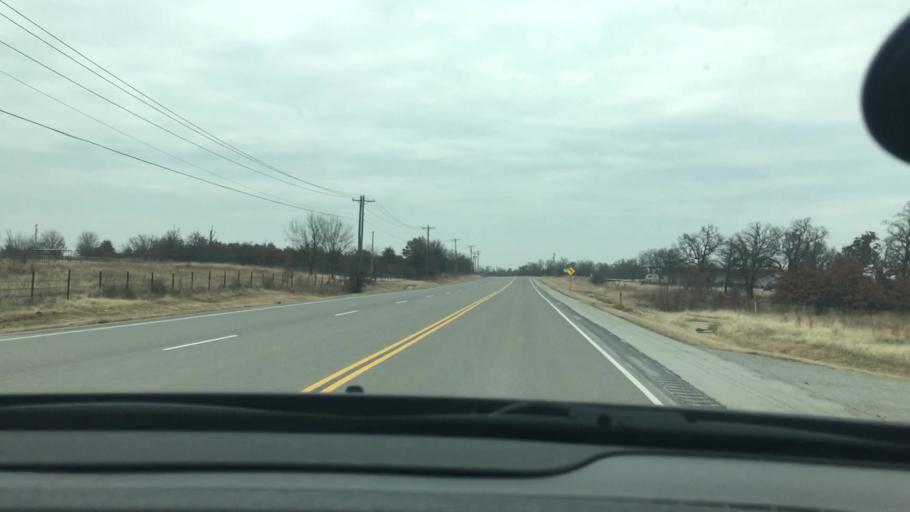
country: US
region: Oklahoma
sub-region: Carter County
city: Healdton
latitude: 34.3955
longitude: -97.5032
